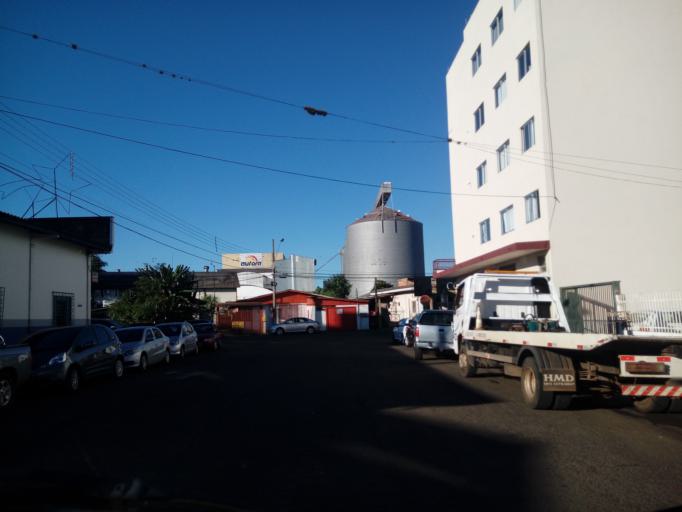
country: BR
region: Santa Catarina
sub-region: Chapeco
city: Chapeco
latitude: -27.0880
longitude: -52.6226
